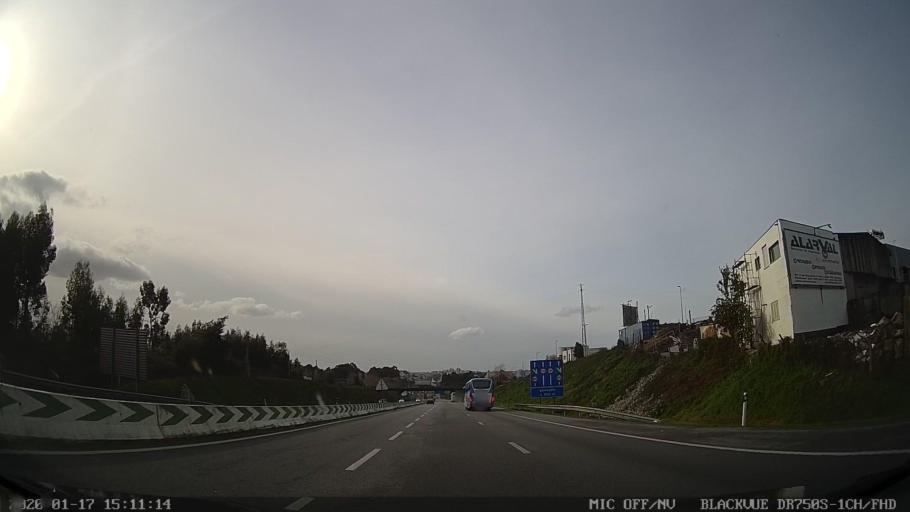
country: PT
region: Porto
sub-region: Gondomar
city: Baguim do Monte
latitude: 41.2011
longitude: -8.5427
